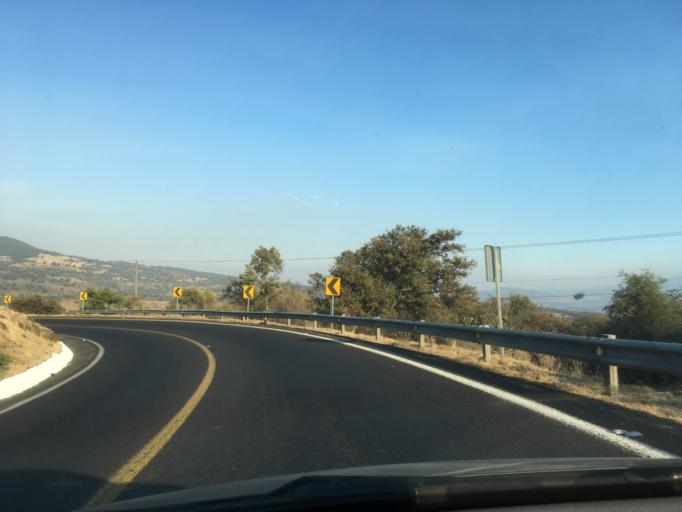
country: MX
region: Michoacan
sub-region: Morelia
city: Iratzio
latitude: 19.6280
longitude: -101.4372
